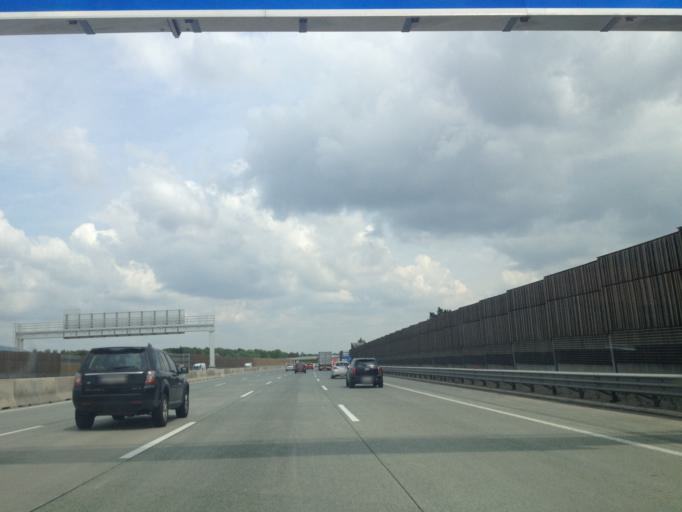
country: AT
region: Lower Austria
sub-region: Politischer Bezirk Baden
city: Kottingbrunn
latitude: 47.9628
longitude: 16.2276
